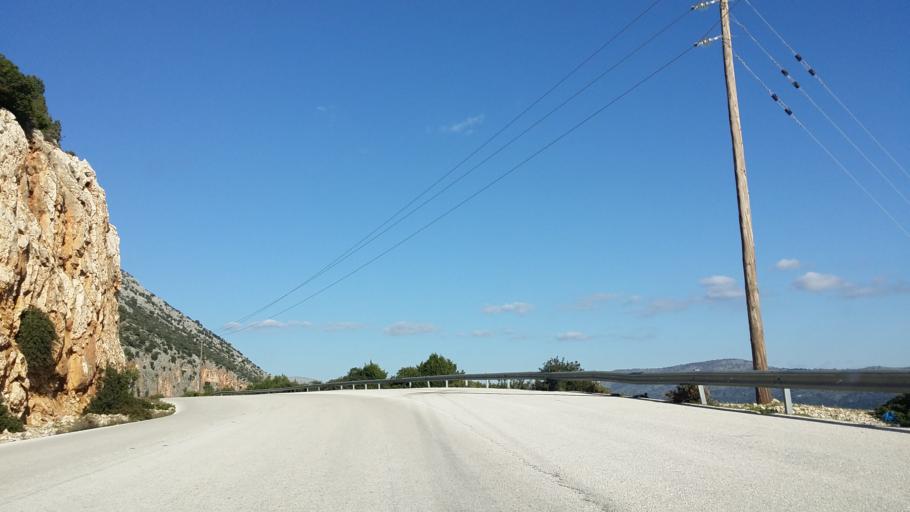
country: GR
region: West Greece
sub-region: Nomos Aitolias kai Akarnanias
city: Astakos
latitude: 38.5068
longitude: 21.0461
